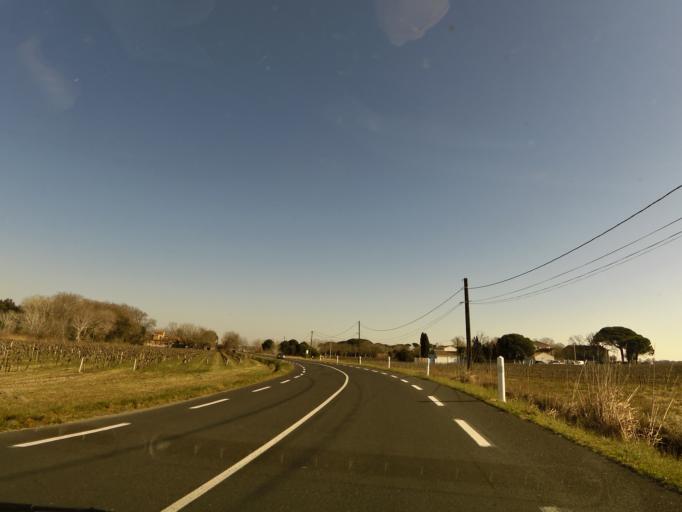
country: FR
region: Languedoc-Roussillon
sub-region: Departement du Gard
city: Aigues-Mortes
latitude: 43.5815
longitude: 4.2535
